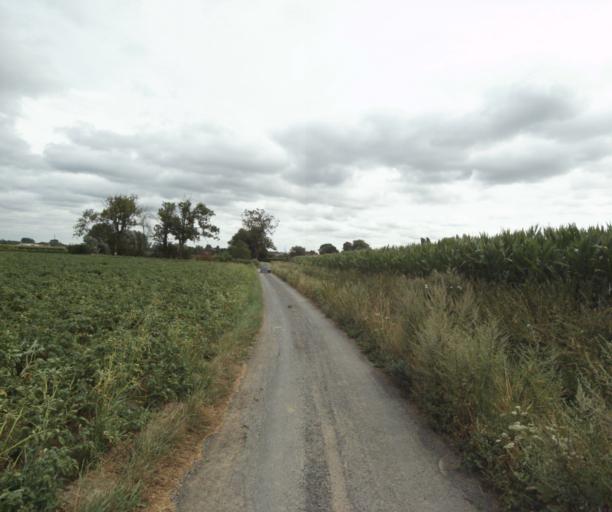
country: FR
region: Nord-Pas-de-Calais
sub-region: Departement du Nord
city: Linselles
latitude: 50.7399
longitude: 3.0954
